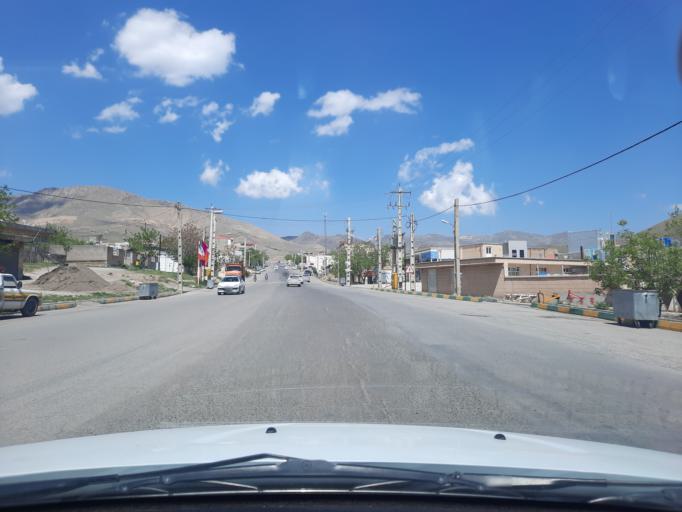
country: IR
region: Qazvin
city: Qazvin
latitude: 36.3308
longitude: 50.1501
